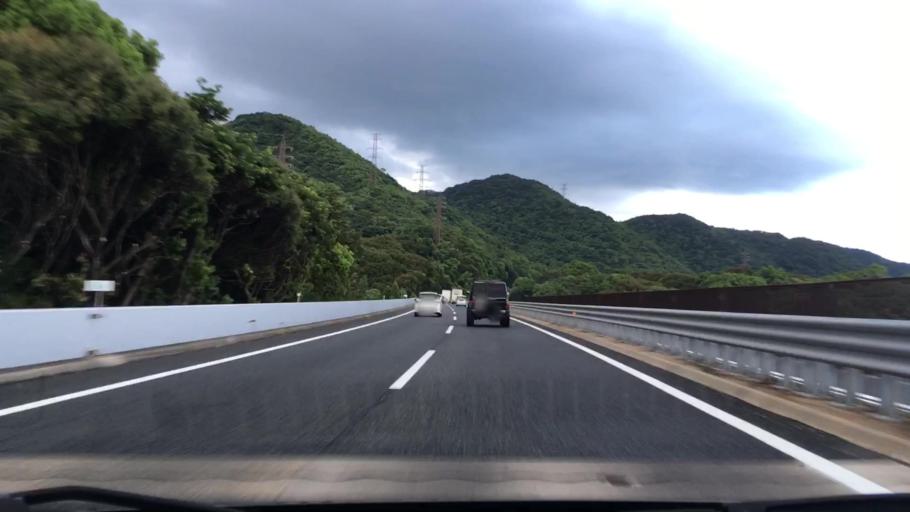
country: JP
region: Fukuoka
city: Kanda
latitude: 33.8567
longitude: 130.9386
